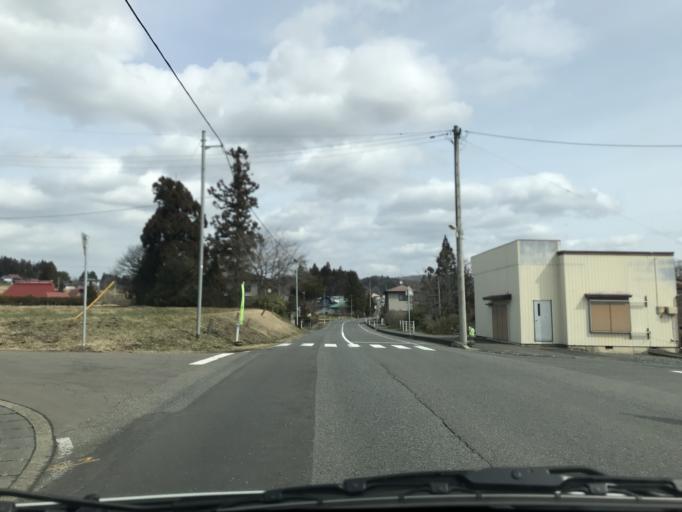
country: JP
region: Iwate
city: Kitakami
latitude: 39.2239
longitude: 141.2341
